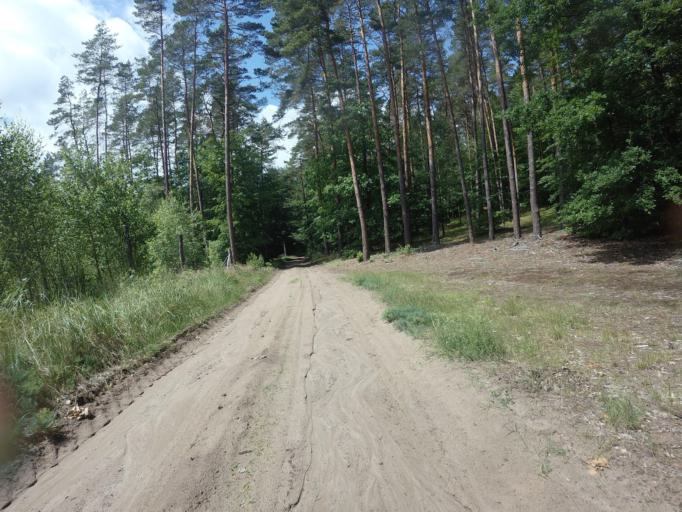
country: PL
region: West Pomeranian Voivodeship
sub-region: Powiat choszczenski
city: Bierzwnik
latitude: 53.0238
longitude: 15.5832
